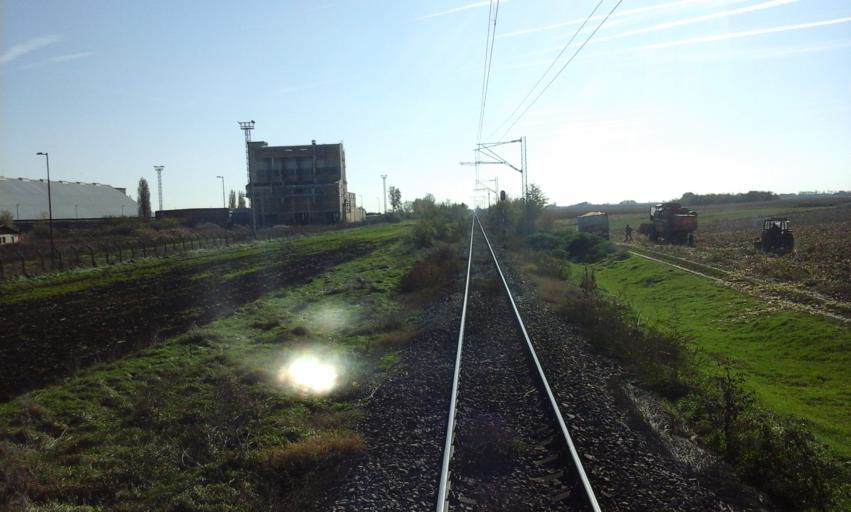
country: RS
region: Autonomna Pokrajina Vojvodina
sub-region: Severnobacki Okrug
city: Subotica
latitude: 46.0060
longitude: 19.6785
